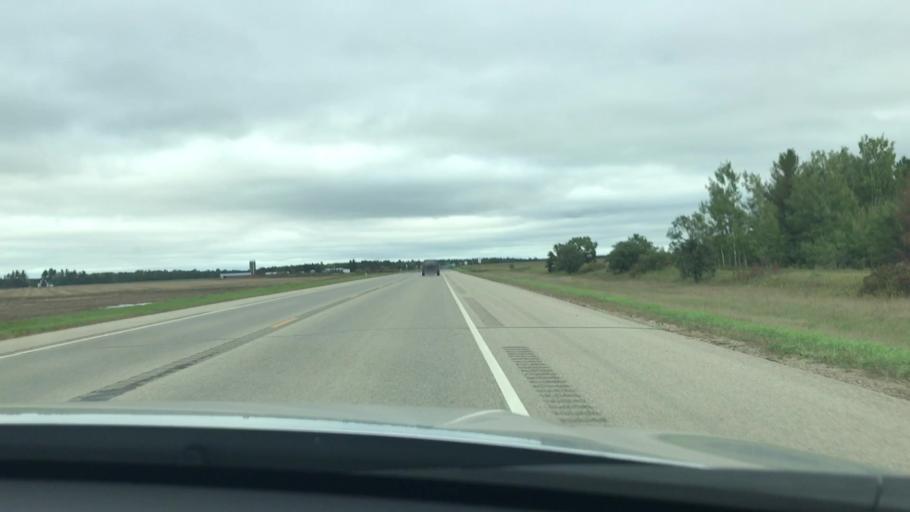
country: US
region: Minnesota
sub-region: Hubbard County
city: Park Rapids
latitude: 46.8543
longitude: -95.0764
